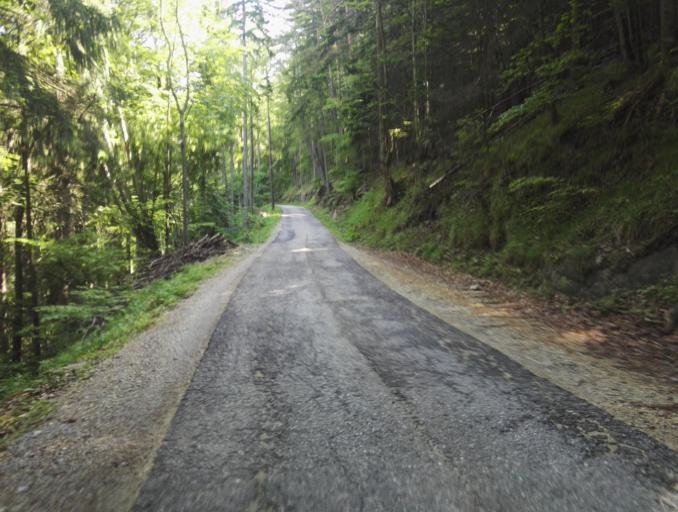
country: AT
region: Styria
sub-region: Politischer Bezirk Graz-Umgebung
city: Semriach
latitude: 47.1850
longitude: 15.4241
